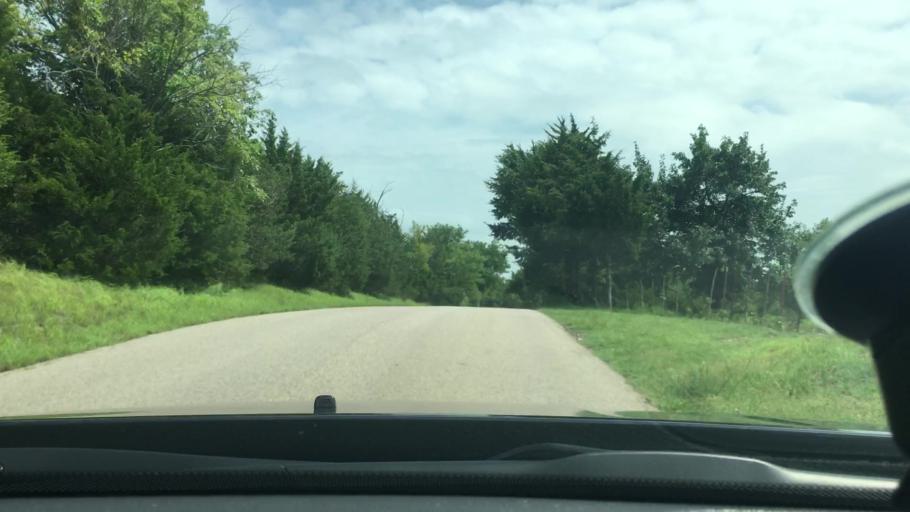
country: US
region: Oklahoma
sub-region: Pontotoc County
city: Ada
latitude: 34.8064
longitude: -96.6991
